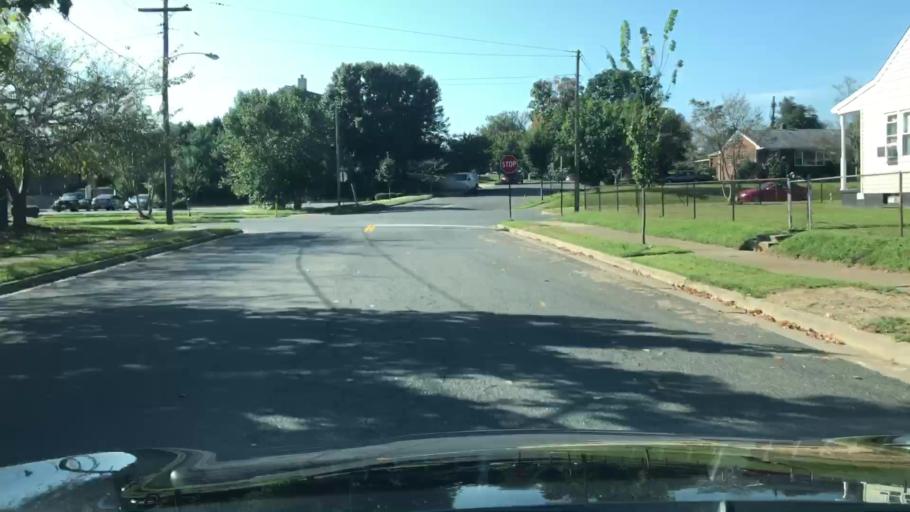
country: US
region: Virginia
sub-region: Stafford County
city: Falmouth
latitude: 38.3190
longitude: -77.4733
